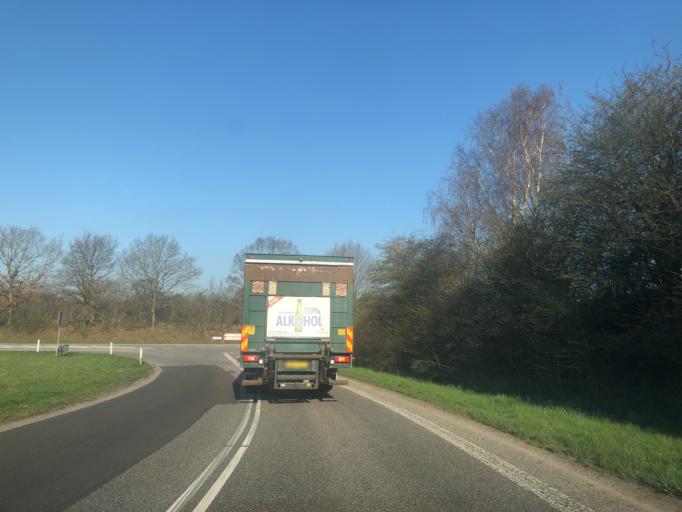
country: DK
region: Zealand
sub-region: Faxe Kommune
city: Fakse
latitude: 55.2575
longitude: 12.0976
